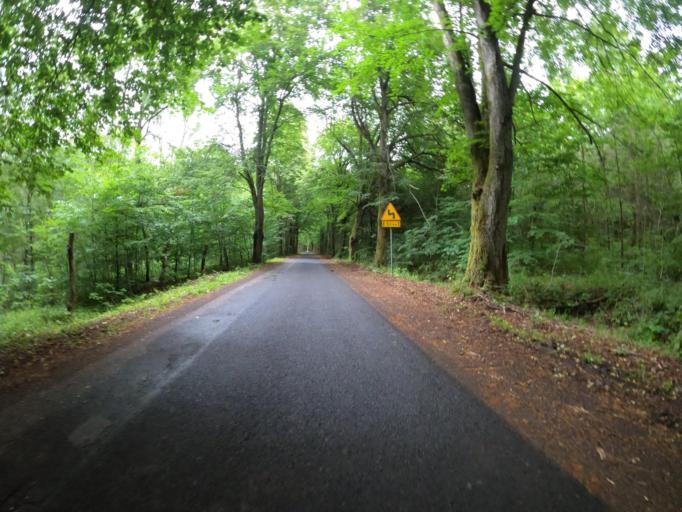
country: PL
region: West Pomeranian Voivodeship
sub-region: Powiat szczecinecki
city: Grzmiaca
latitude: 53.9471
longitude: 16.4675
